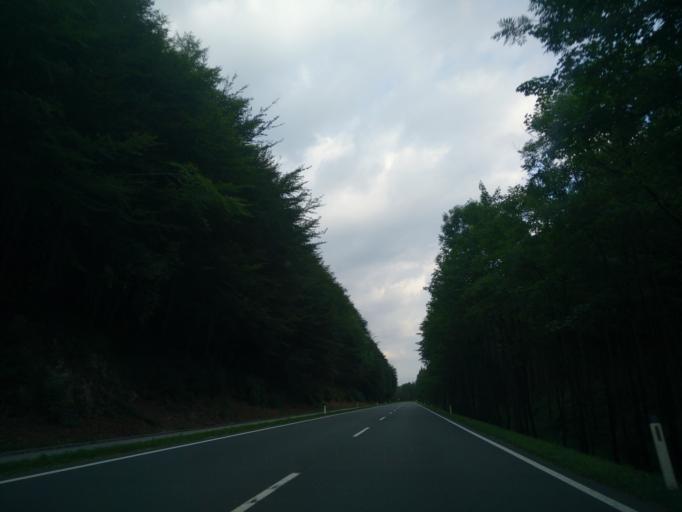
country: AT
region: Salzburg
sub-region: Politischer Bezirk Salzburg-Umgebung
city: Fuschl am See
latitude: 47.7980
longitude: 13.3228
